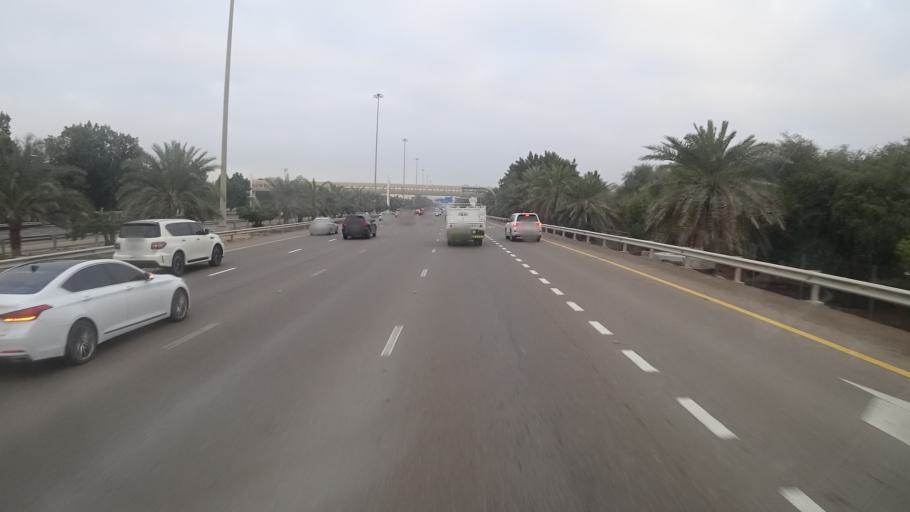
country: AE
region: Abu Dhabi
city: Abu Dhabi
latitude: 24.3631
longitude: 54.5633
